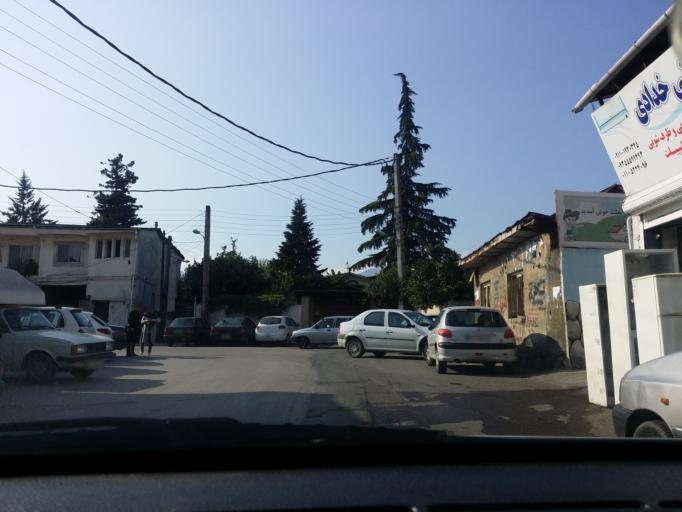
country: IR
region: Mazandaran
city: Chalus
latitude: 36.6560
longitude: 51.4159
